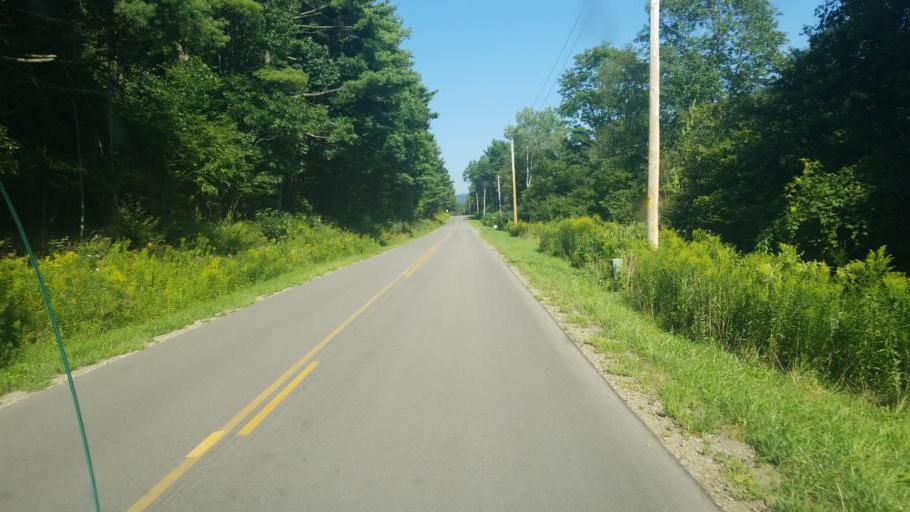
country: US
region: New York
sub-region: Allegany County
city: Wellsville
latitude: 42.0102
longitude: -78.0366
